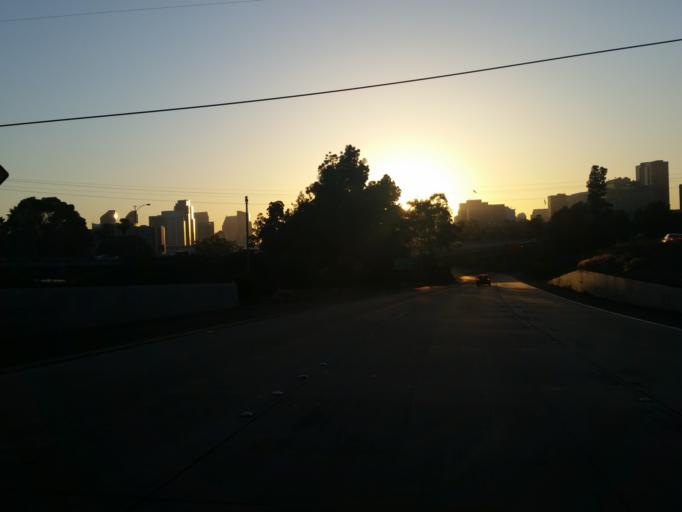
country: US
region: California
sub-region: San Diego County
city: San Diego
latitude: 32.7134
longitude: -117.1446
